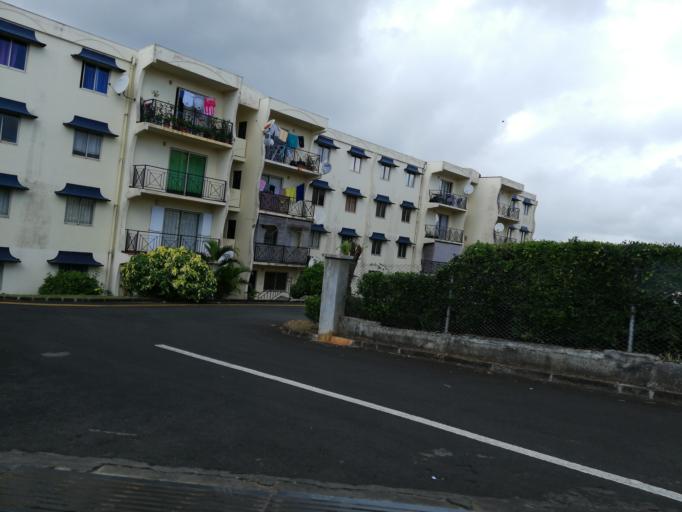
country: MU
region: Moka
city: Moka
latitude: -20.2150
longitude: 57.4756
